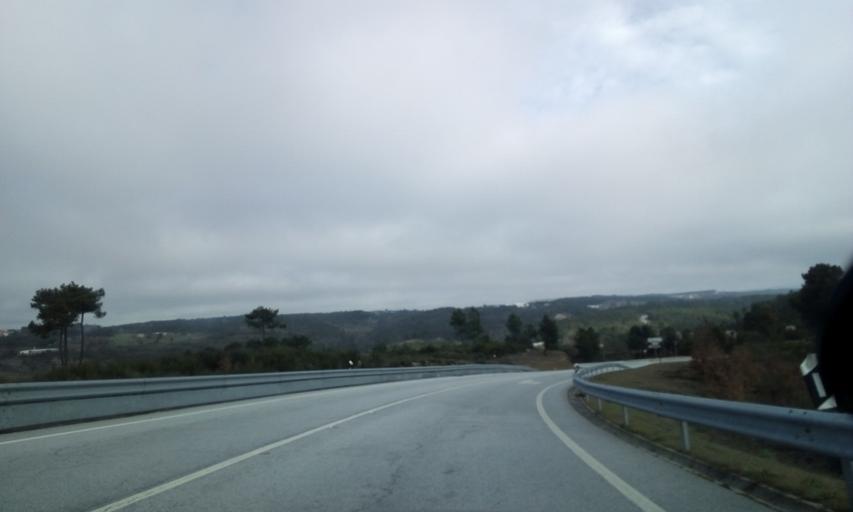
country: PT
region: Guarda
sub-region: Aguiar da Beira
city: Aguiar da Beira
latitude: 40.7726
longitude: -7.5047
